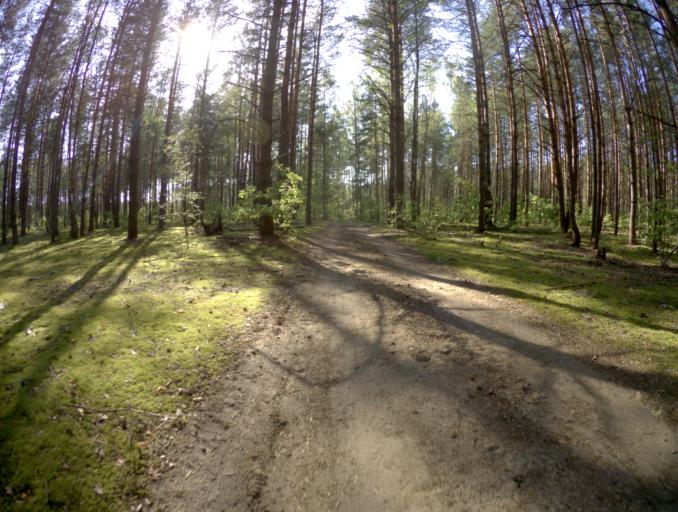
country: RU
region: Vladimir
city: Petushki
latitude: 55.8953
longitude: 39.4599
